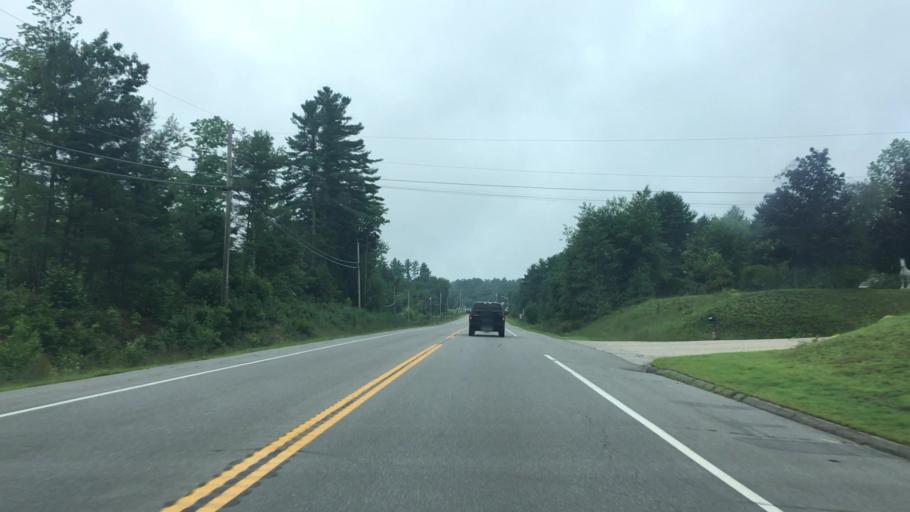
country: US
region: Maine
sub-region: York County
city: Lebanon
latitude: 43.4267
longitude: -70.8423
